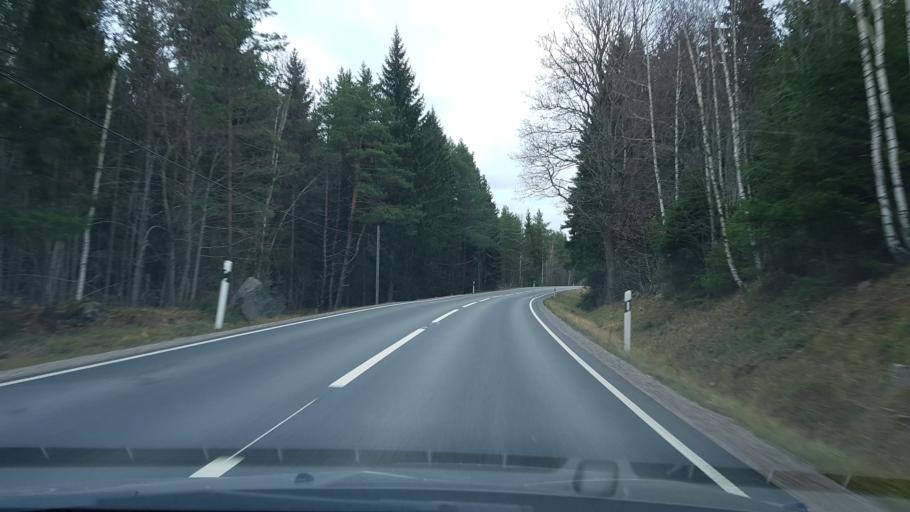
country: SE
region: Stockholm
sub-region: Norrtalje Kommun
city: Skanninge
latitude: 60.0105
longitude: 18.3344
